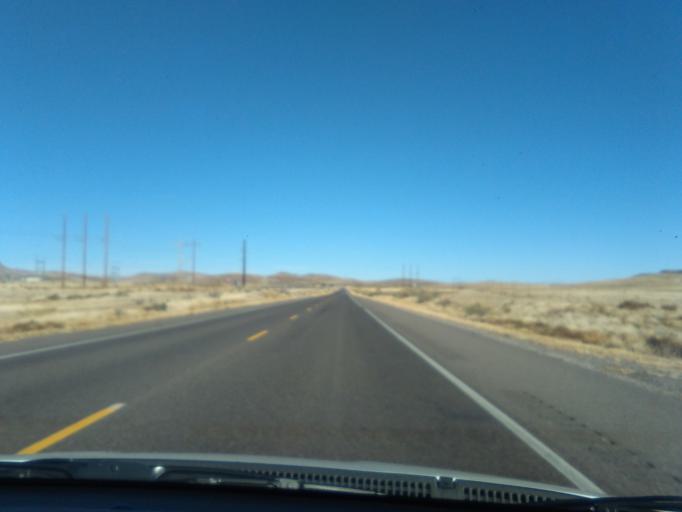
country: US
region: New Mexico
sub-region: Dona Ana County
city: Hatch
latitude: 32.5620
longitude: -107.4683
